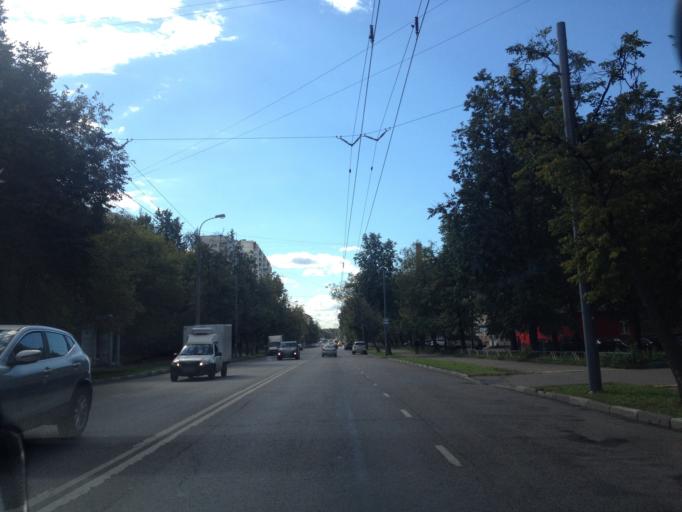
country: RU
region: Moscow
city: Metrogorodok
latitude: 55.8014
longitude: 37.7990
